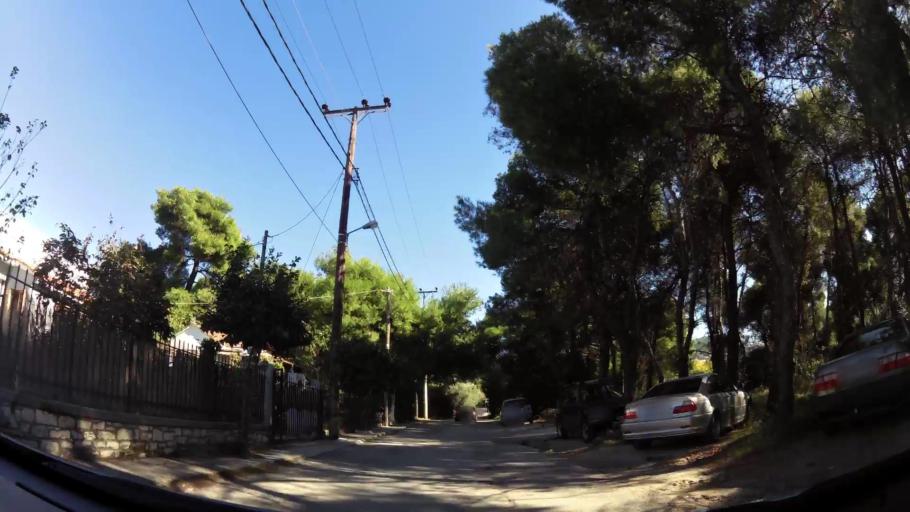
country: GR
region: Attica
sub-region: Nomarchia Athinas
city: Nea Erythraia
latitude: 38.1079
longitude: 23.8203
